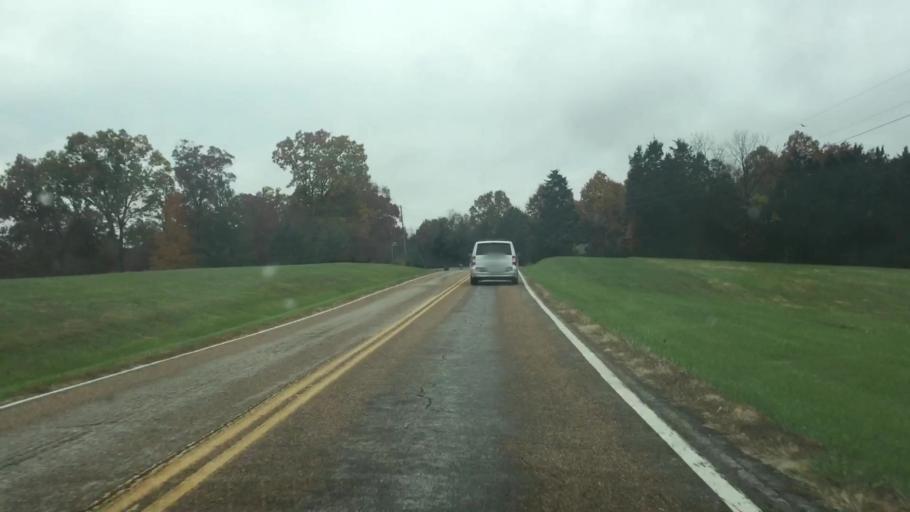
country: US
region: Missouri
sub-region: Callaway County
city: Fulton
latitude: 38.7385
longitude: -91.7055
